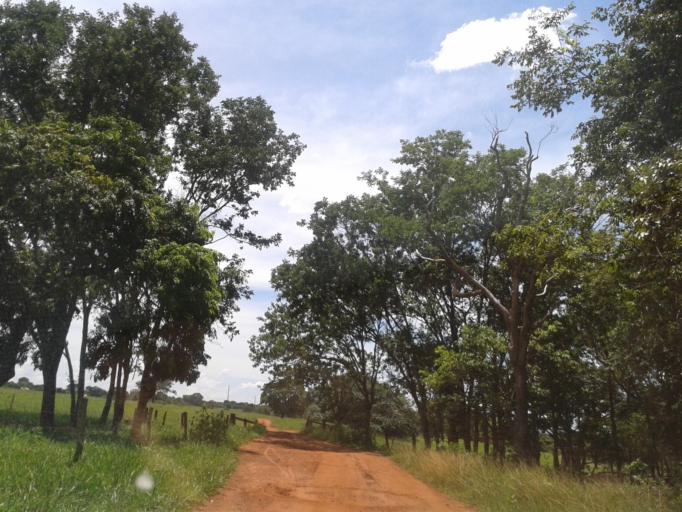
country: BR
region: Minas Gerais
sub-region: Capinopolis
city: Capinopolis
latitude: -18.8014
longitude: -49.7754
